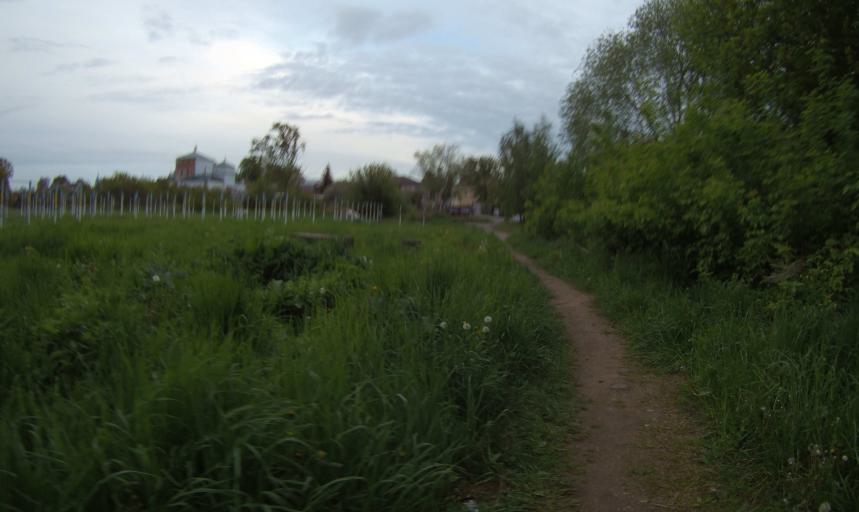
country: RU
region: Moskovskaya
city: Kolomna
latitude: 55.1072
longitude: 38.7724
